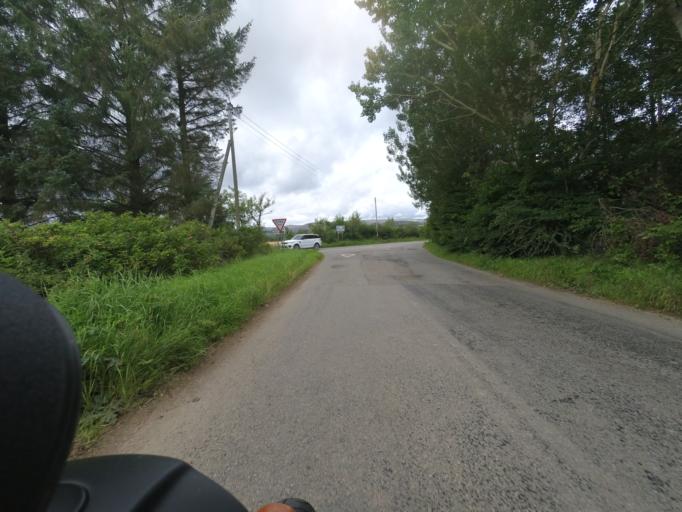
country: GB
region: Scotland
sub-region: Aberdeenshire
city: Laurencekirk
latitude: 56.8409
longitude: -2.5675
